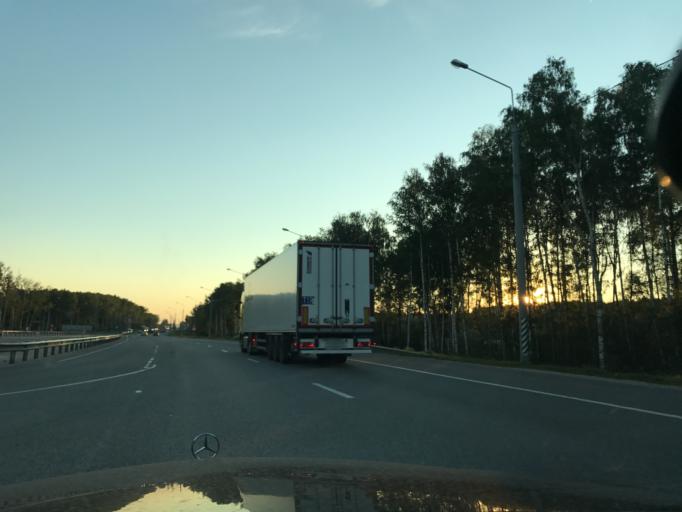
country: RU
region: Vladimir
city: Petushki
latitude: 55.9454
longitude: 39.5133
